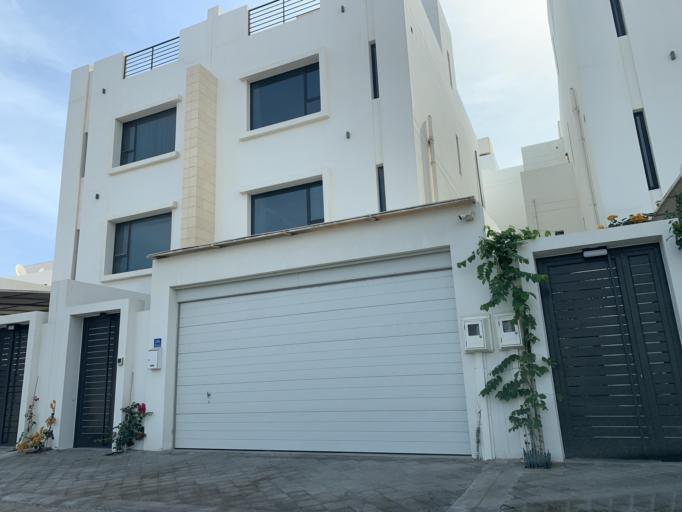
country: BH
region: Central Governorate
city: Madinat Hamad
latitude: 26.1295
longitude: 50.4716
